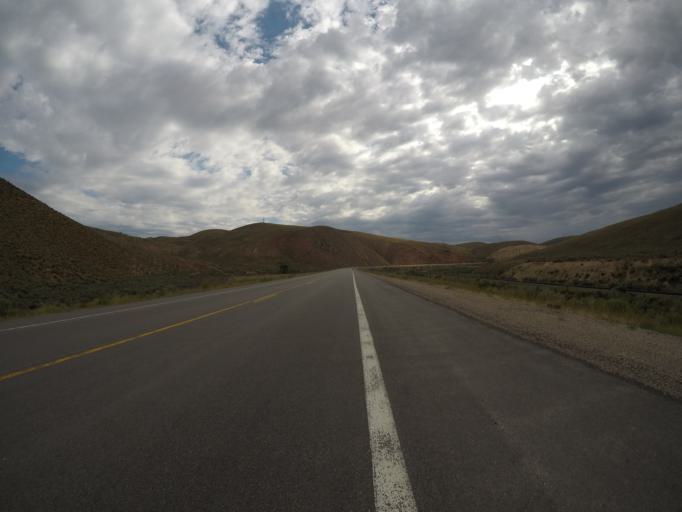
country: US
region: Wyoming
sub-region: Lincoln County
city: Kemmerer
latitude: 41.8241
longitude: -110.8174
